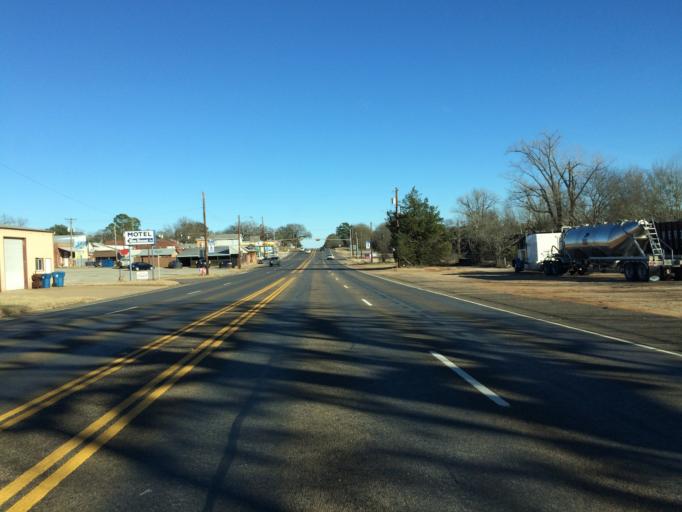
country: US
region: Texas
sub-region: Wood County
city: Hawkins
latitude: 32.5877
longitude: -95.2118
